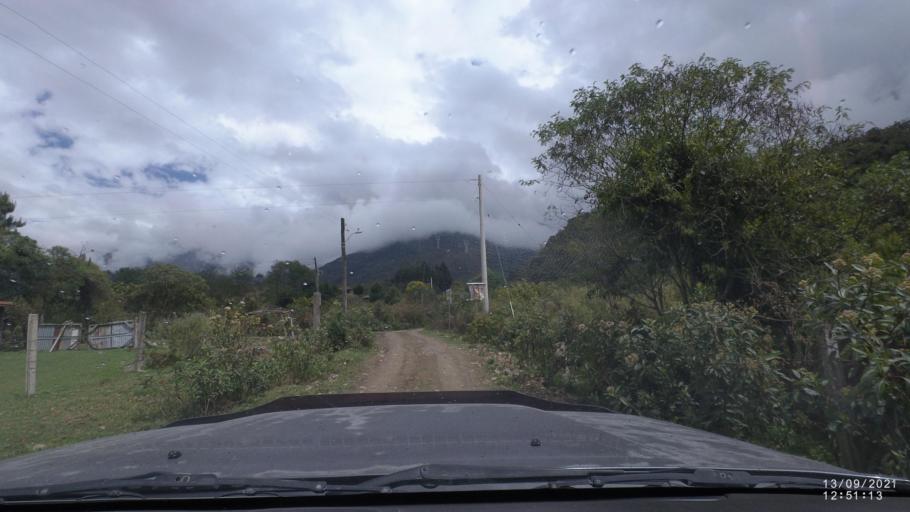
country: BO
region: Cochabamba
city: Colomi
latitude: -17.2393
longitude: -65.8204
